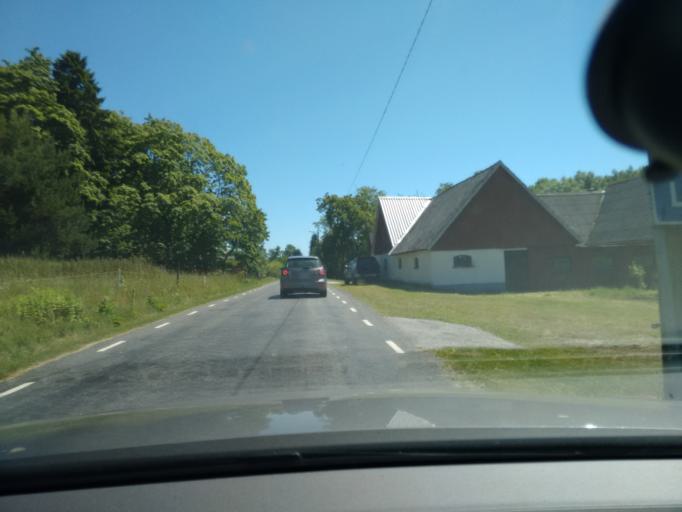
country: SE
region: Skane
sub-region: Kristianstads Kommun
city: Degeberga
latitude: 55.7786
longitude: 14.0930
